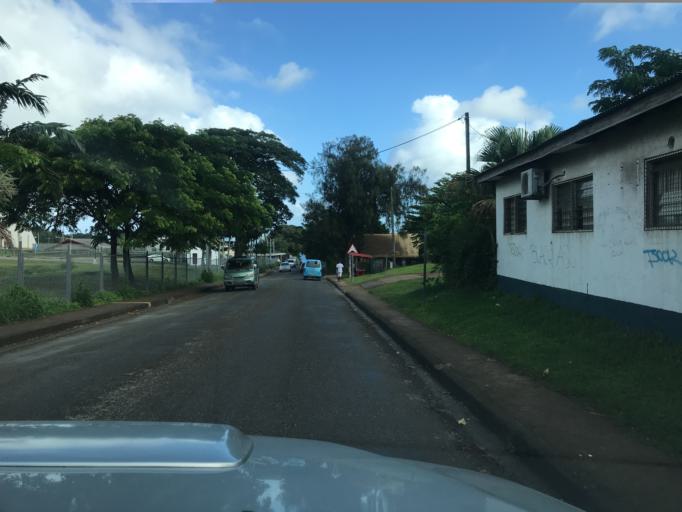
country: VU
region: Shefa
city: Port-Vila
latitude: -17.7429
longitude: 168.3172
